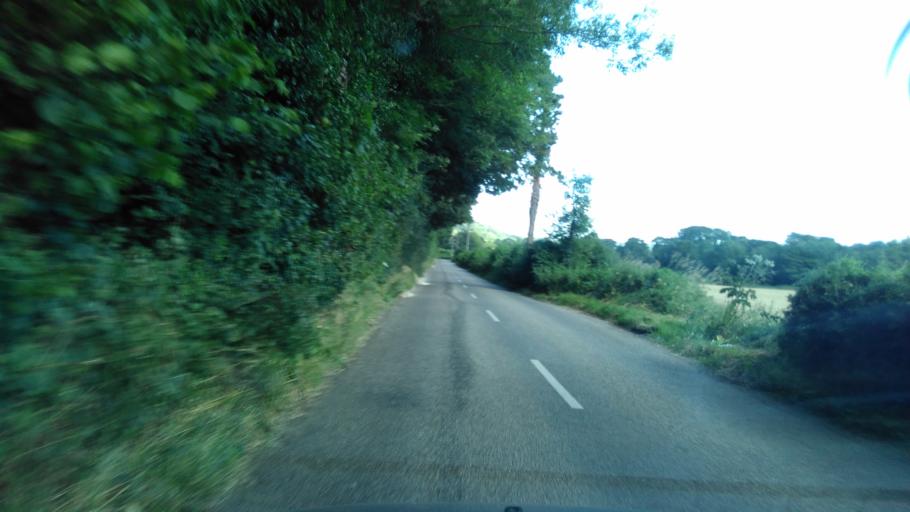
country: GB
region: England
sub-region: Kent
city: Dunkirk
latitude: 51.2490
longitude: 0.9620
